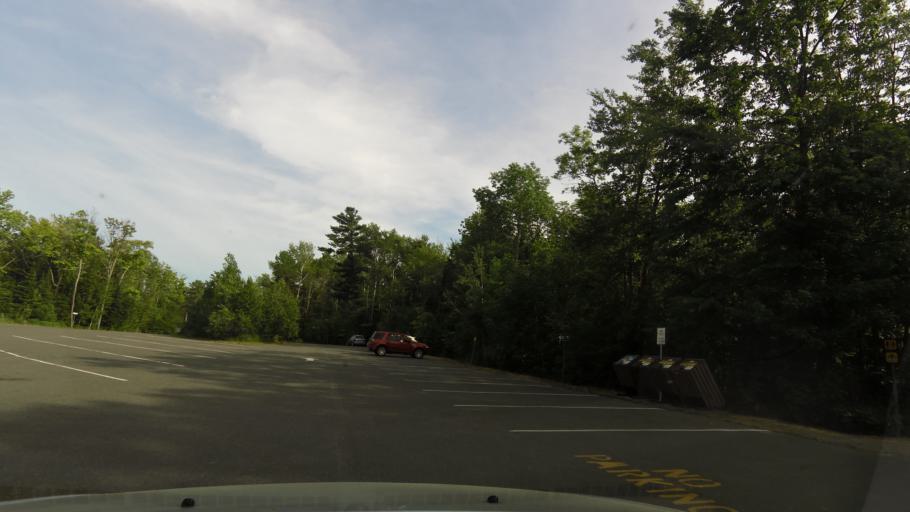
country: CA
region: Ontario
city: Greater Sudbury
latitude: 46.0161
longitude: -80.5848
